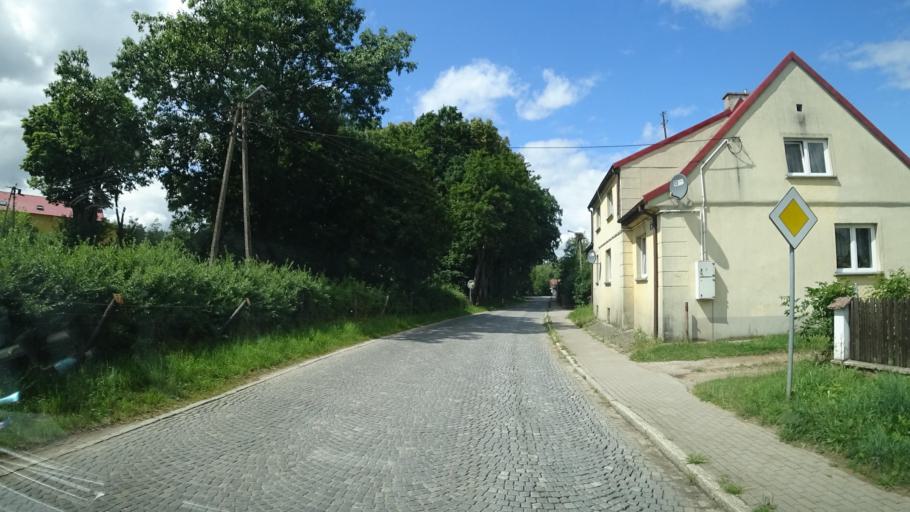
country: PL
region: Warmian-Masurian Voivodeship
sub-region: Powiat goldapski
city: Banie Mazurskie
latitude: 54.2174
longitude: 22.1544
